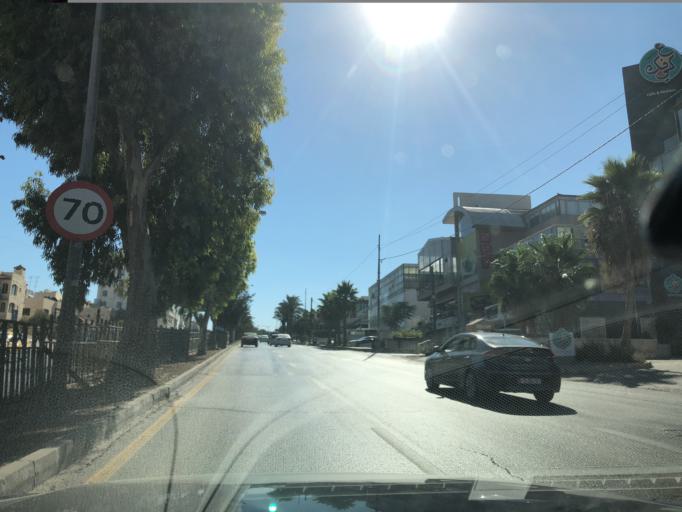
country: JO
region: Amman
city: Al Jubayhah
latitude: 31.9739
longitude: 35.8683
